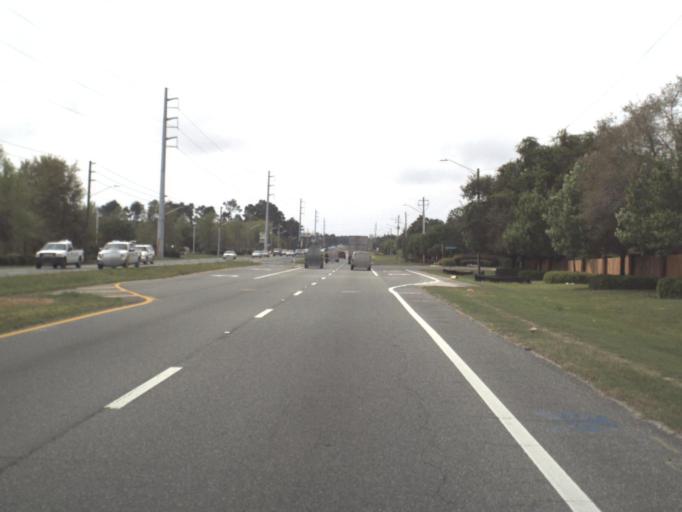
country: US
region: Florida
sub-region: Santa Rosa County
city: Oriole Beach
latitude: 30.3798
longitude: -87.1125
